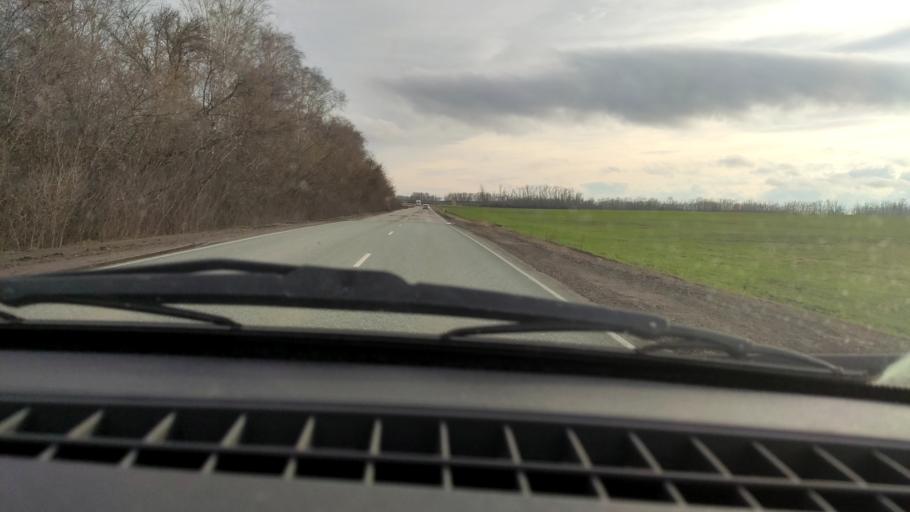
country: RU
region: Bashkortostan
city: Chishmy
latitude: 54.4975
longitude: 55.2807
